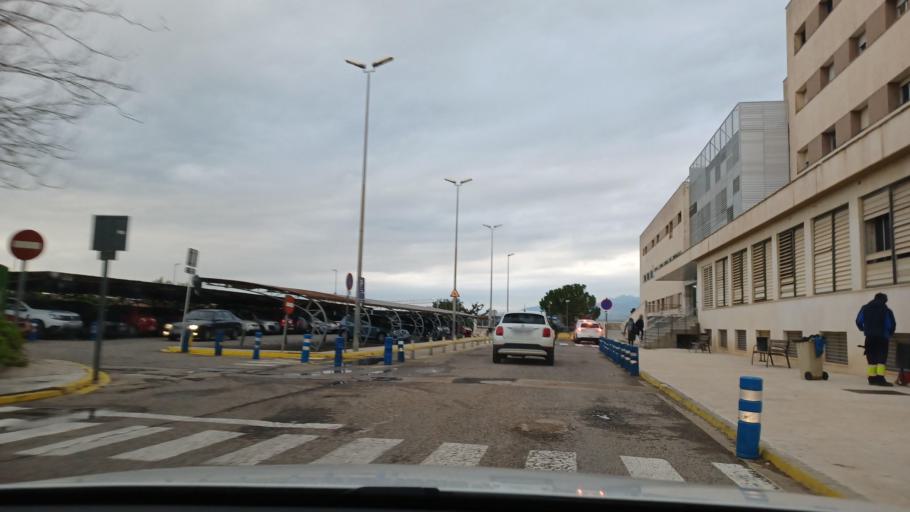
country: ES
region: Catalonia
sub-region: Provincia de Tarragona
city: Tortosa
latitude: 40.8112
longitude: 0.5251
